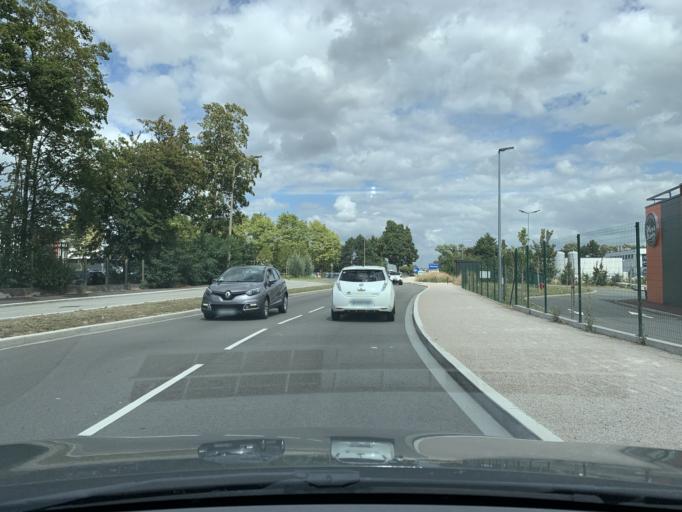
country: FR
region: Nord-Pas-de-Calais
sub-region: Departement du Pas-de-Calais
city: Henin-Beaumont
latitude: 50.3999
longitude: 2.9749
